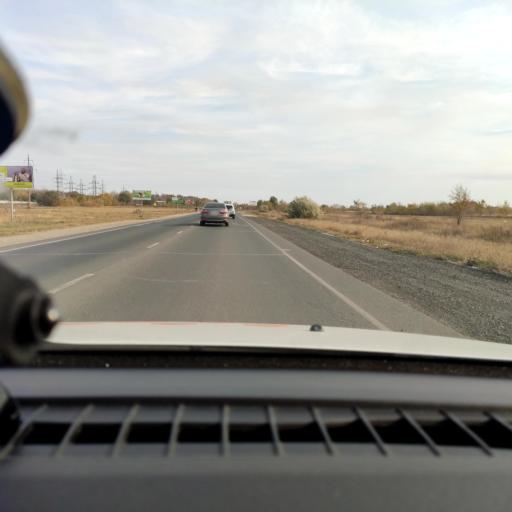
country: RU
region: Samara
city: Samara
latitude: 53.1283
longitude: 50.1608
